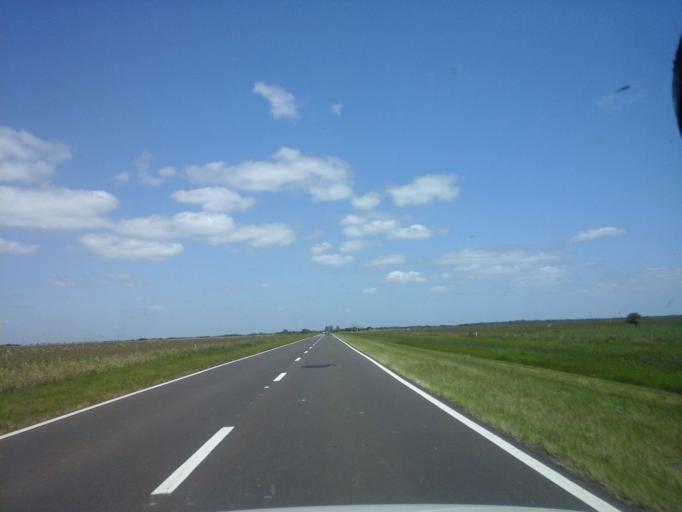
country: PY
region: Neembucu
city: Cerrito
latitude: -27.3780
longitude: -57.8264
